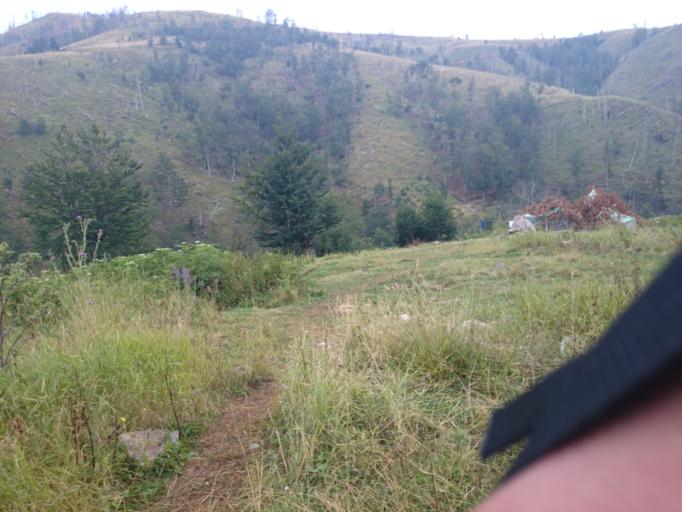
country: AL
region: Lezhe
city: Kurbnesh
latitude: 41.7855
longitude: 20.1482
